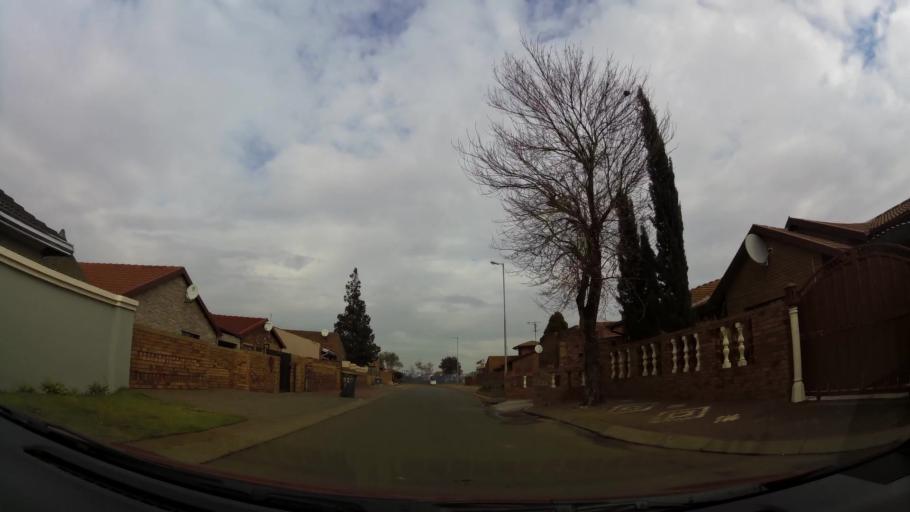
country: ZA
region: Gauteng
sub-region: City of Johannesburg Metropolitan Municipality
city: Soweto
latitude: -26.2708
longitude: 27.8358
